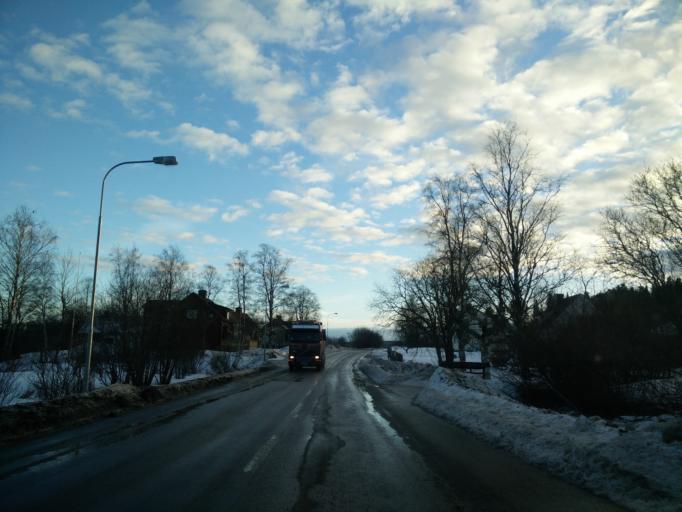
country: SE
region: Vaesternorrland
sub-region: Sundsvalls Kommun
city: Njurundabommen
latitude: 62.2606
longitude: 17.3777
